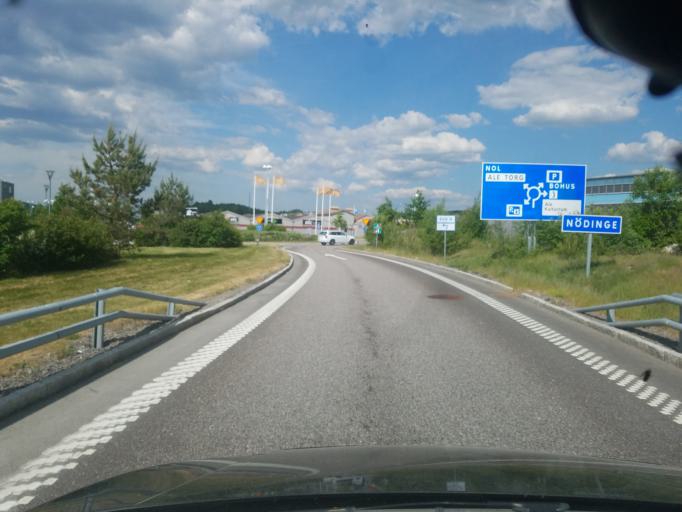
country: SE
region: Vaestra Goetaland
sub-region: Ale Kommun
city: Nodinge-Nol
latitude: 57.8915
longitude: 12.0442
